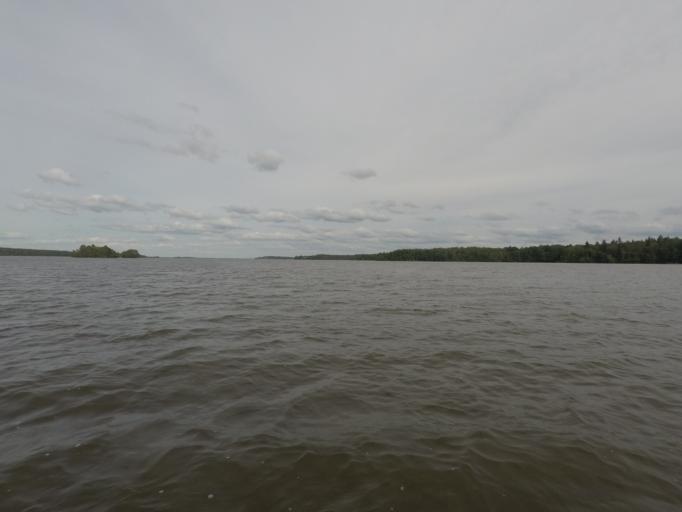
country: SE
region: Soedermanland
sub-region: Eskilstuna Kommun
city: Kvicksund
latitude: 59.4555
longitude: 16.3645
